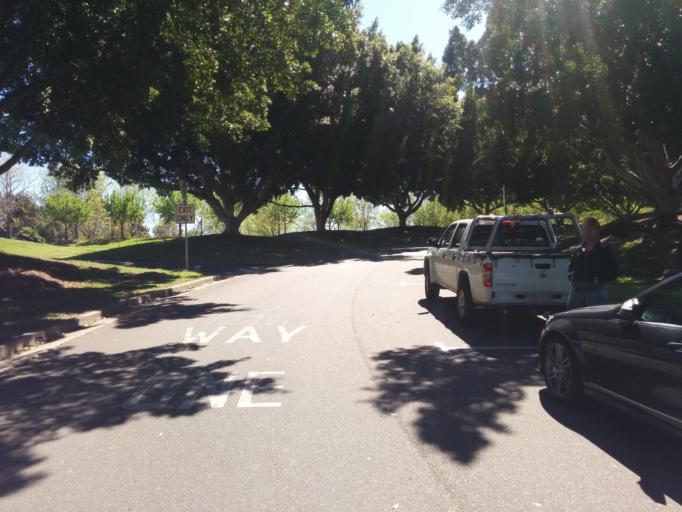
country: AU
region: New South Wales
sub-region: Canada Bay
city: Concord West
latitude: -33.8498
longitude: 151.0758
